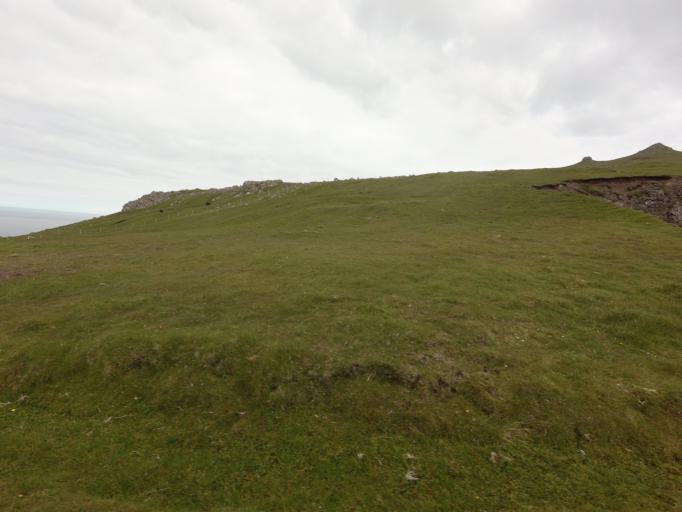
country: FO
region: Suduroy
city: Vagur
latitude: 61.4279
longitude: -6.7527
